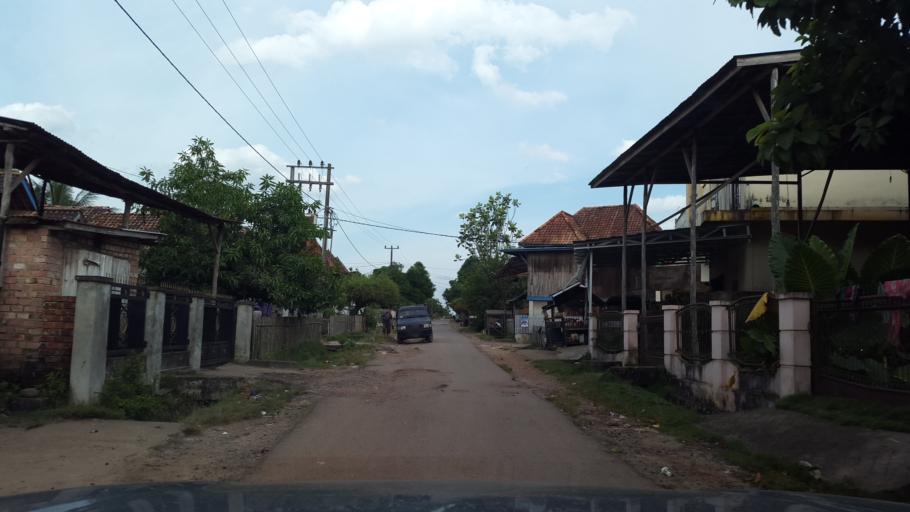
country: ID
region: South Sumatra
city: Glumbang
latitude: -3.4213
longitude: 104.4877
